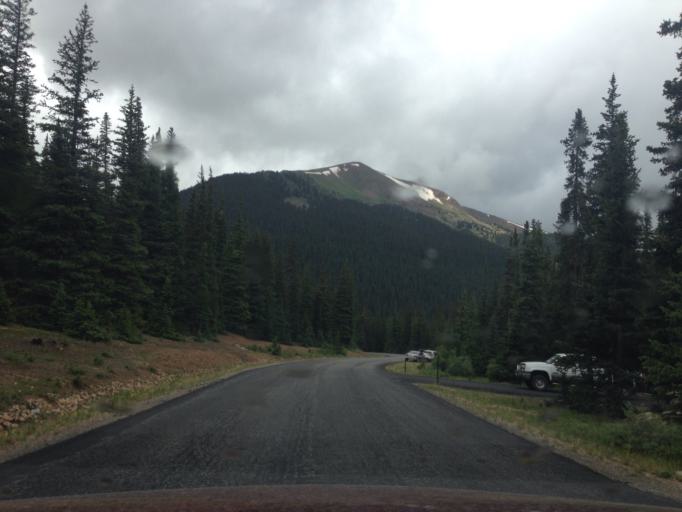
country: US
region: Colorado
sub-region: Clear Creek County
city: Georgetown
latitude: 39.6069
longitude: -105.7132
